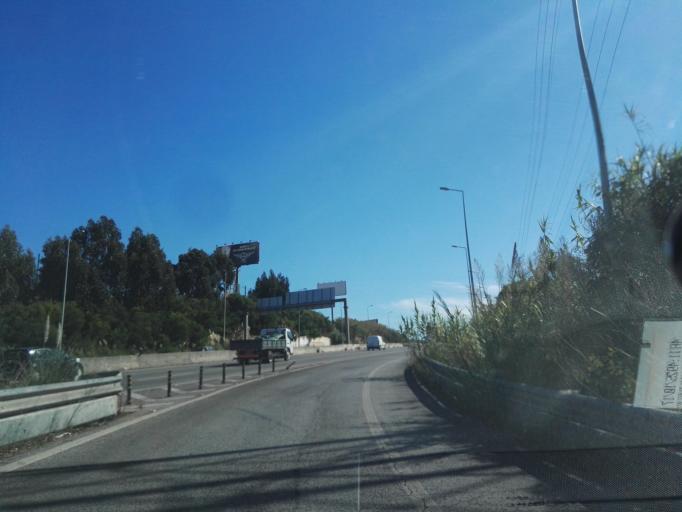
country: PT
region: Lisbon
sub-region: Sintra
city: Rio de Mouro
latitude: 38.7755
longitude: -9.3218
